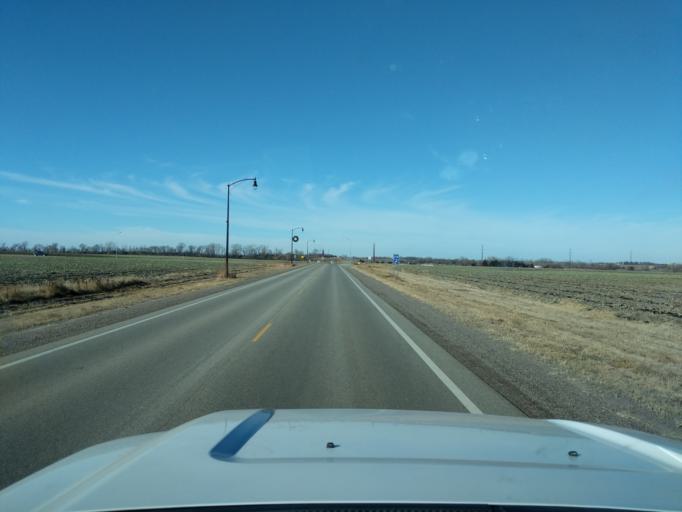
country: US
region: Minnesota
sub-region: Yellow Medicine County
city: Granite Falls
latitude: 44.7691
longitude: -95.5405
